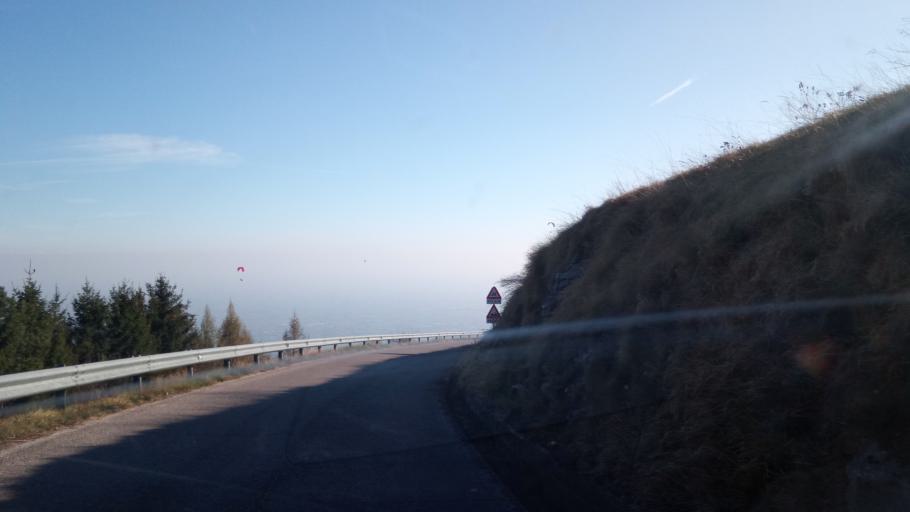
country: IT
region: Veneto
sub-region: Provincia di Treviso
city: Borso del Grappa
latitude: 45.8265
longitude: 11.7689
